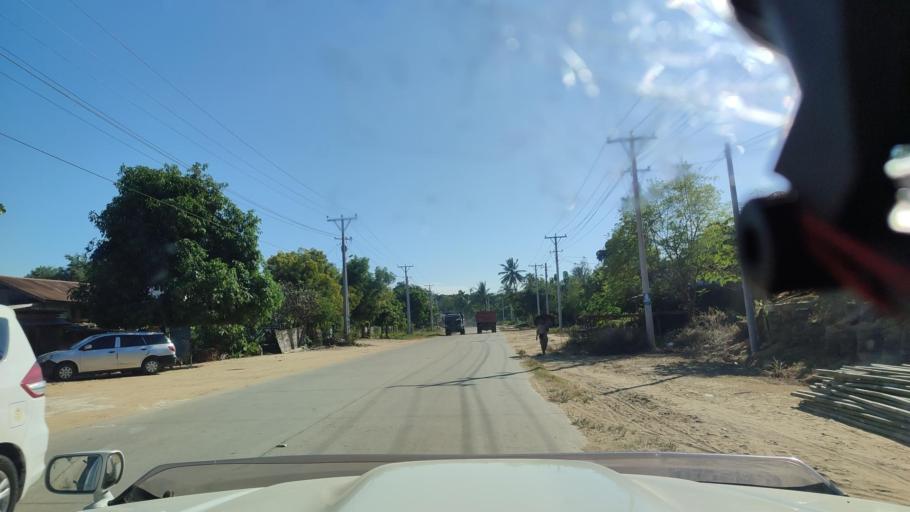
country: MM
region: Mandalay
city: Nay Pyi Taw
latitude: 19.9081
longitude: 96.0243
